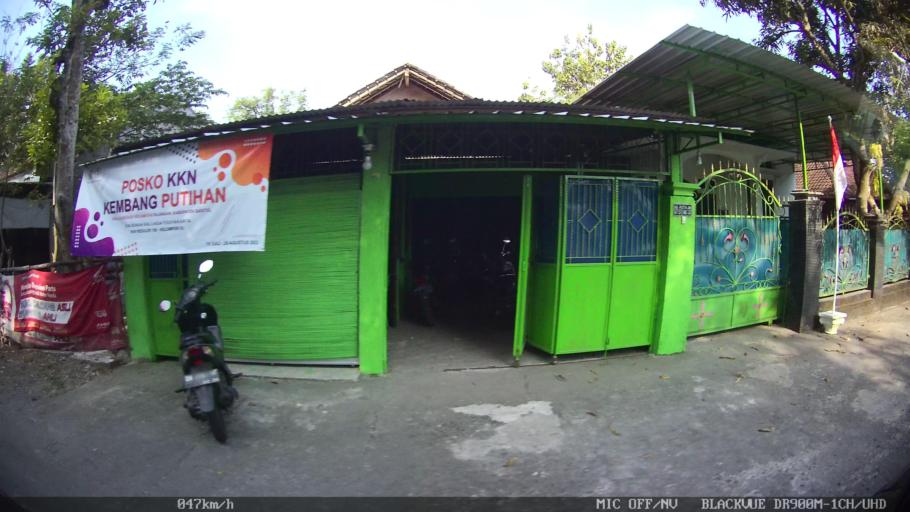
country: ID
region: Daerah Istimewa Yogyakarta
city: Bantul
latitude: -7.8631
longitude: 110.3188
